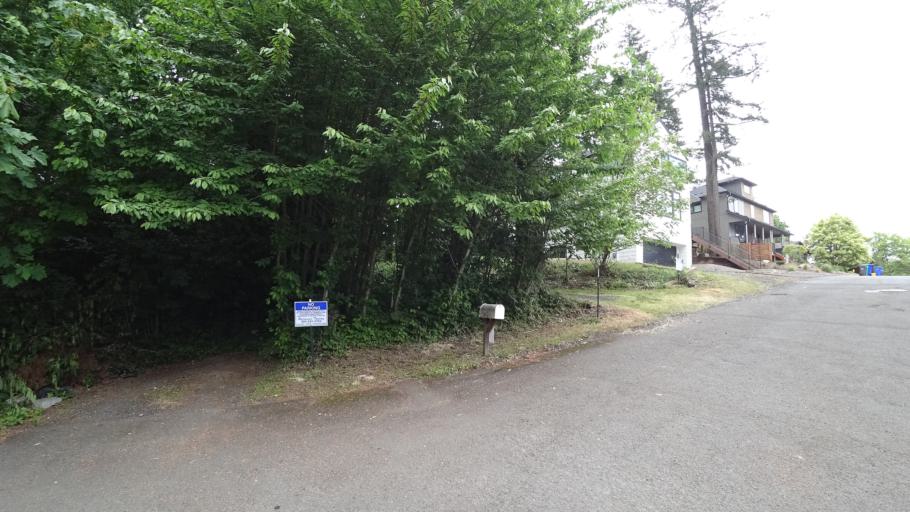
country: US
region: Oregon
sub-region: Washington County
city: Garden Home-Whitford
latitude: 45.4573
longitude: -122.7254
